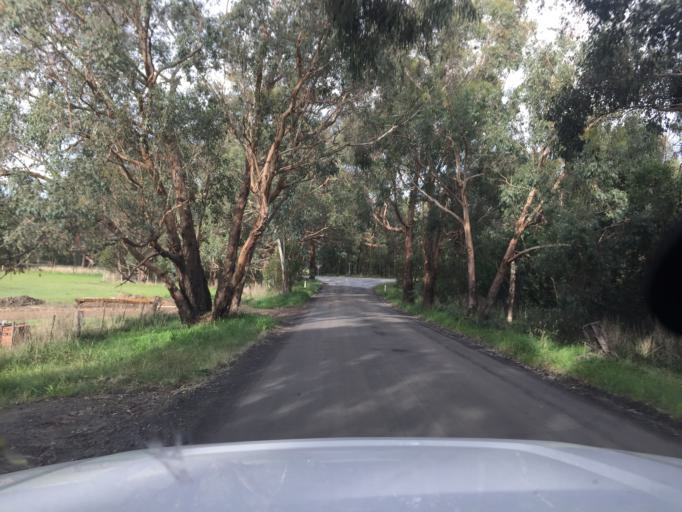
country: AU
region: Victoria
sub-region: Yarra Ranges
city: Healesville
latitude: -37.6508
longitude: 145.4701
